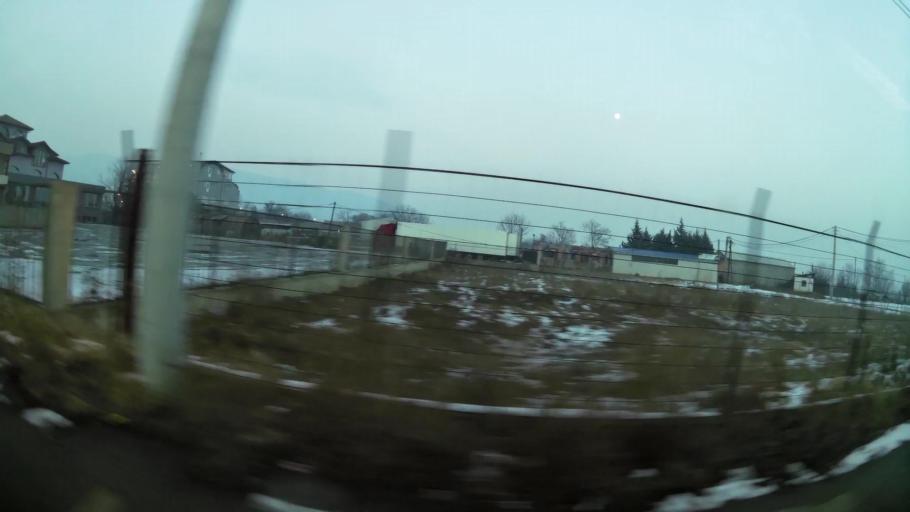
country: MK
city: Creshevo
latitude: 42.0130
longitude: 21.5203
